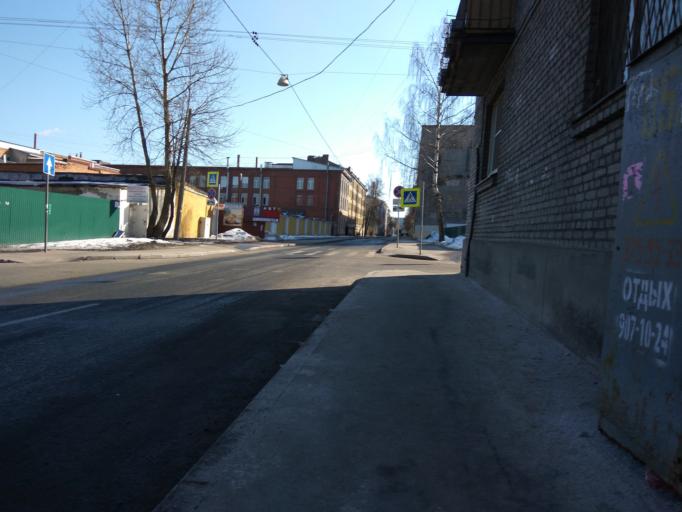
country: RU
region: St.-Petersburg
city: Admiralteisky
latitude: 59.8923
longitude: 30.3246
